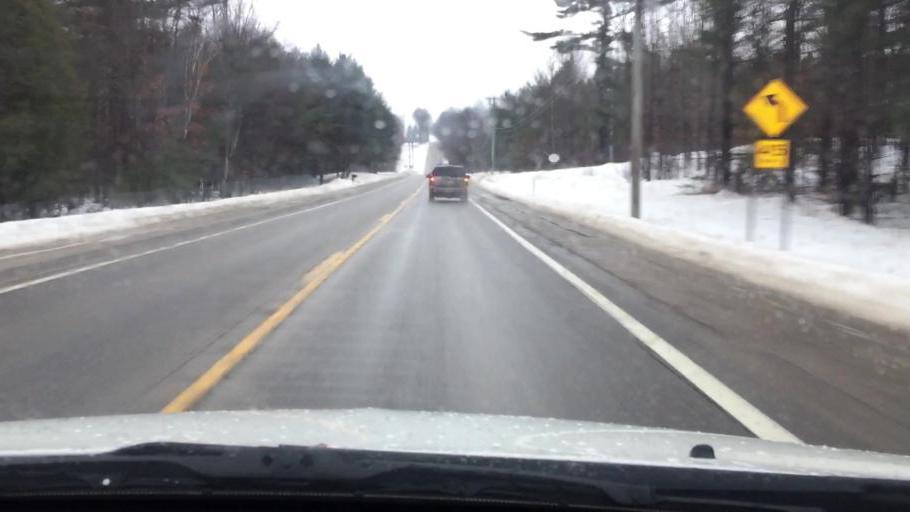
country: US
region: Michigan
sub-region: Charlevoix County
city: East Jordan
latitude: 45.2300
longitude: -85.1817
